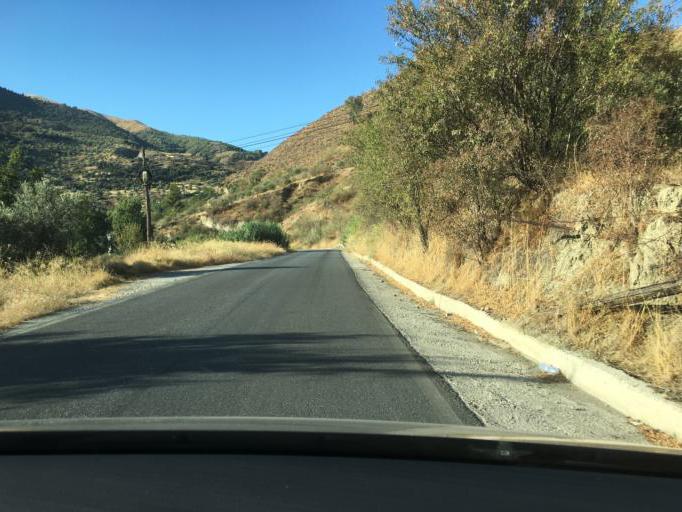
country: ES
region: Andalusia
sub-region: Provincia de Granada
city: Pinos Genil
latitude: 37.1667
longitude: -3.5159
